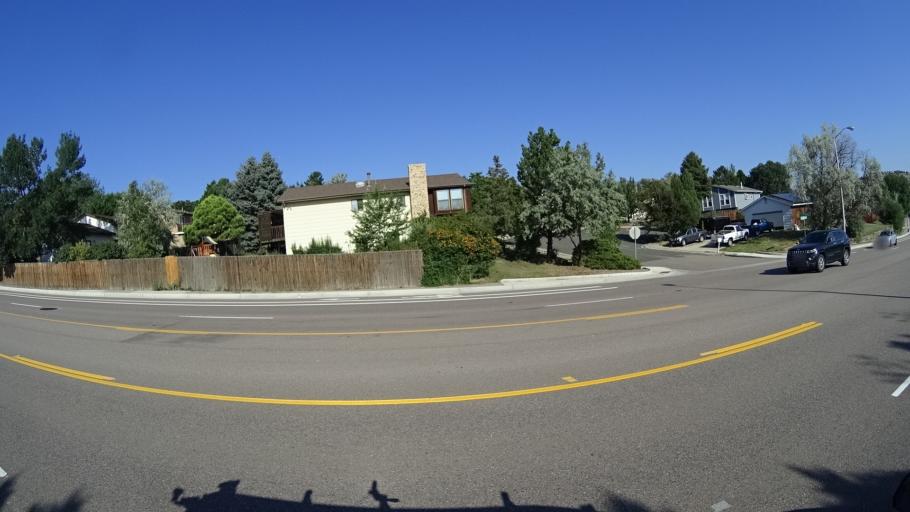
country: US
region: Colorado
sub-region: El Paso County
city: Colorado Springs
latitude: 38.8855
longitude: -104.8471
